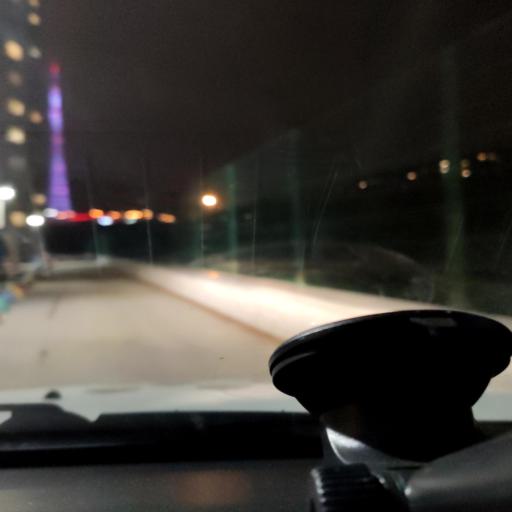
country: RU
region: Perm
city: Perm
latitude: 58.0113
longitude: 56.3026
